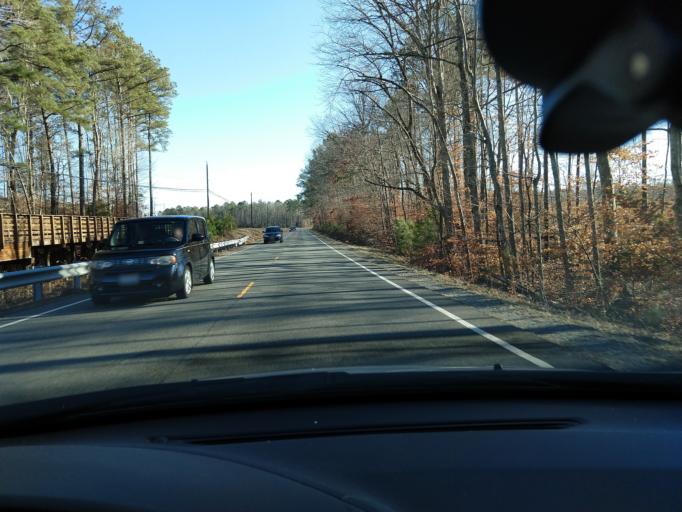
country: US
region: Virginia
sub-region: Charles City County
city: Charles City
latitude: 37.3194
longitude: -76.9719
